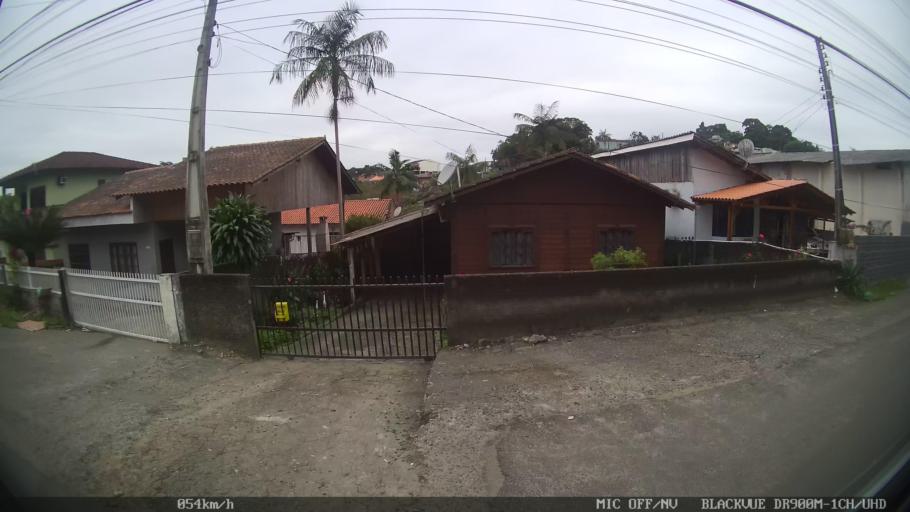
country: BR
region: Santa Catarina
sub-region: Joinville
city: Joinville
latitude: -26.3547
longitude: -48.8201
